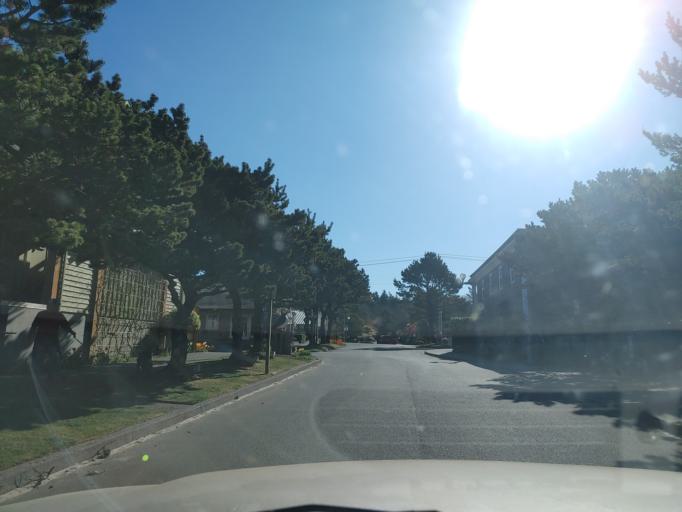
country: US
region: Oregon
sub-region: Clatsop County
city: Cannon Beach
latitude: 45.8900
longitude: -123.9627
